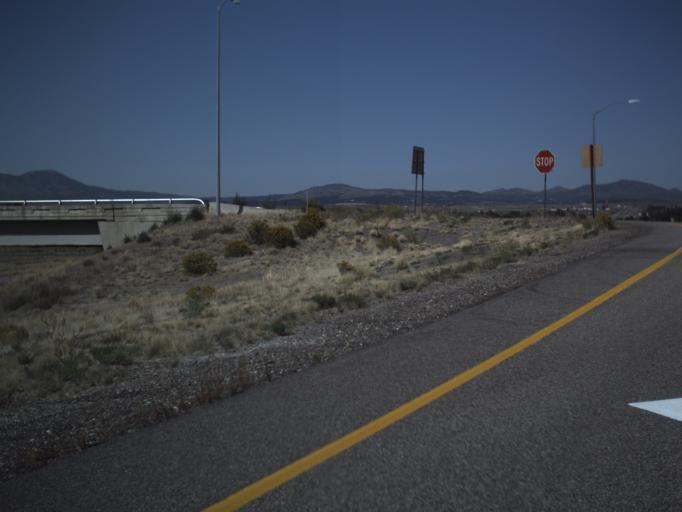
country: US
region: Utah
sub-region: Beaver County
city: Beaver
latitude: 38.2485
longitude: -112.6492
